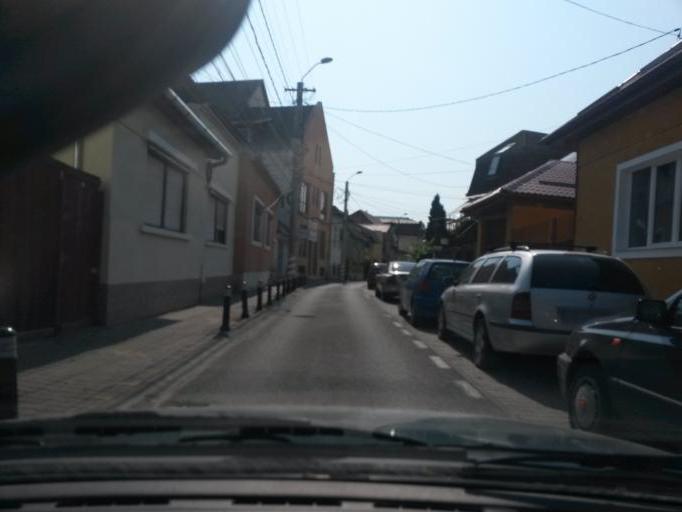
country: RO
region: Mures
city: Targu-Mures
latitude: 46.5491
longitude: 24.5565
